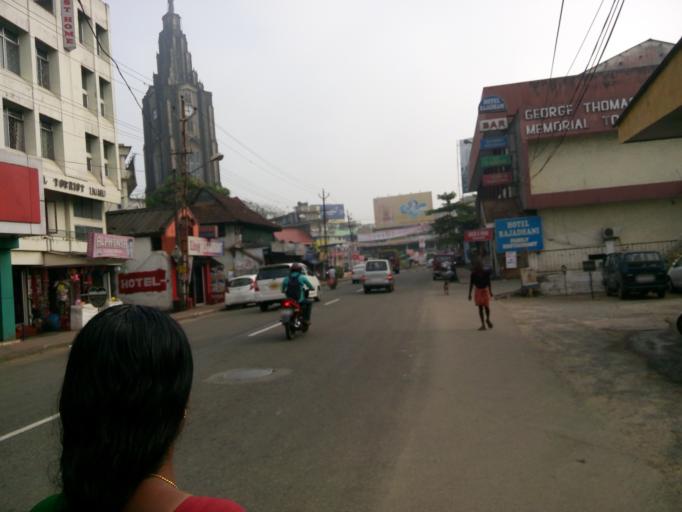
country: IN
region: Kerala
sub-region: Kottayam
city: Lalam
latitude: 9.7122
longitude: 76.6825
